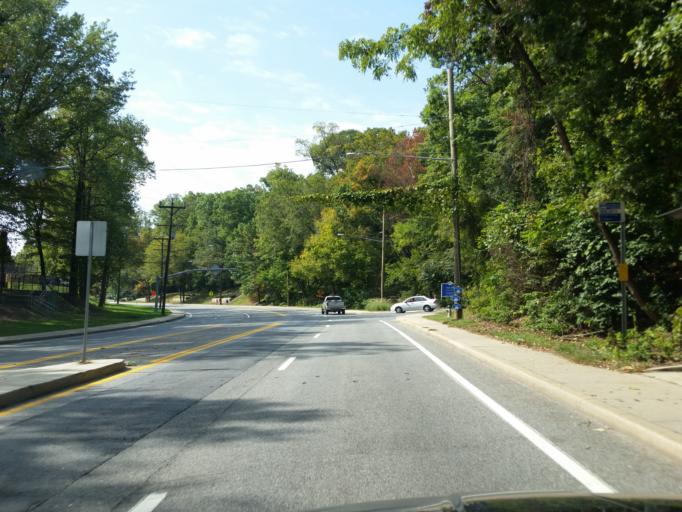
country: US
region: Maryland
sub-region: Prince George's County
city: Langley Park
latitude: 39.0013
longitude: -76.9875
